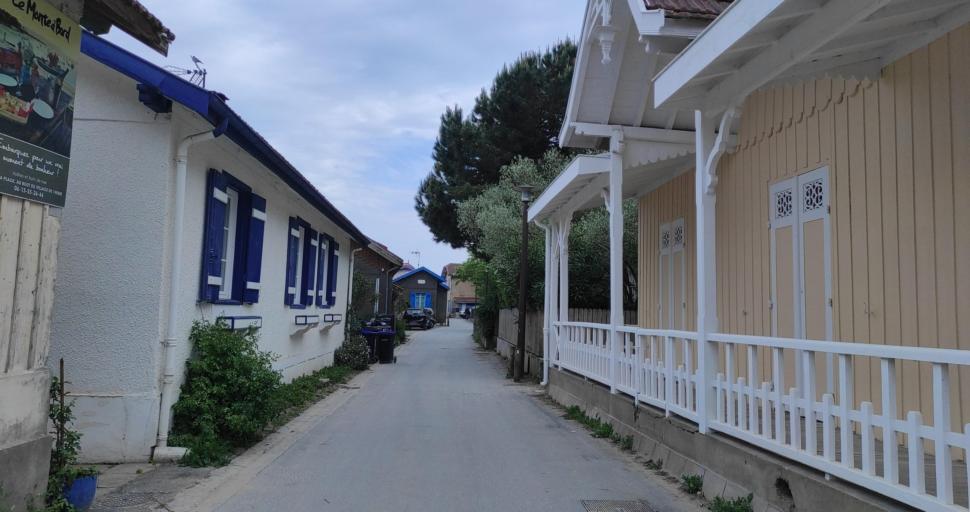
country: FR
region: Aquitaine
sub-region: Departement de la Gironde
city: Arcachon
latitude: 44.6919
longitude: -1.2329
